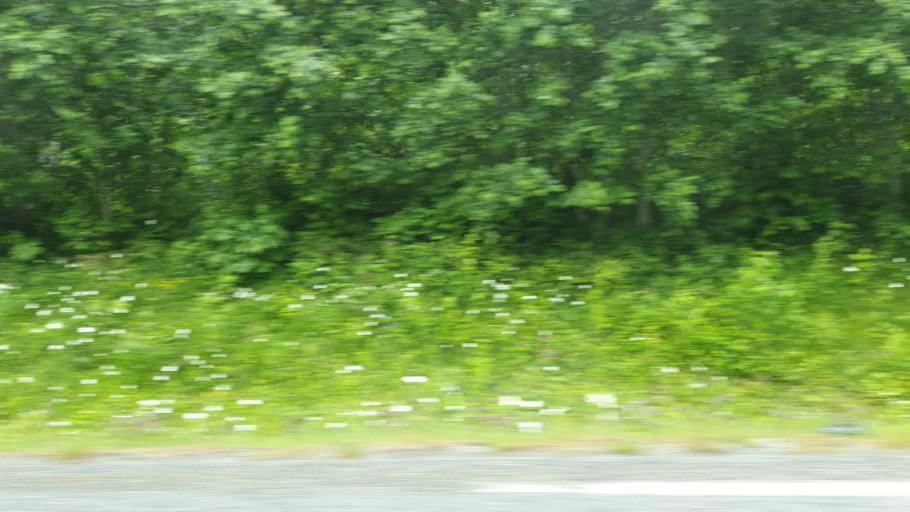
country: NO
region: Oppland
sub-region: Dovre
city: Dovre
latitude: 61.8520
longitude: 9.2855
